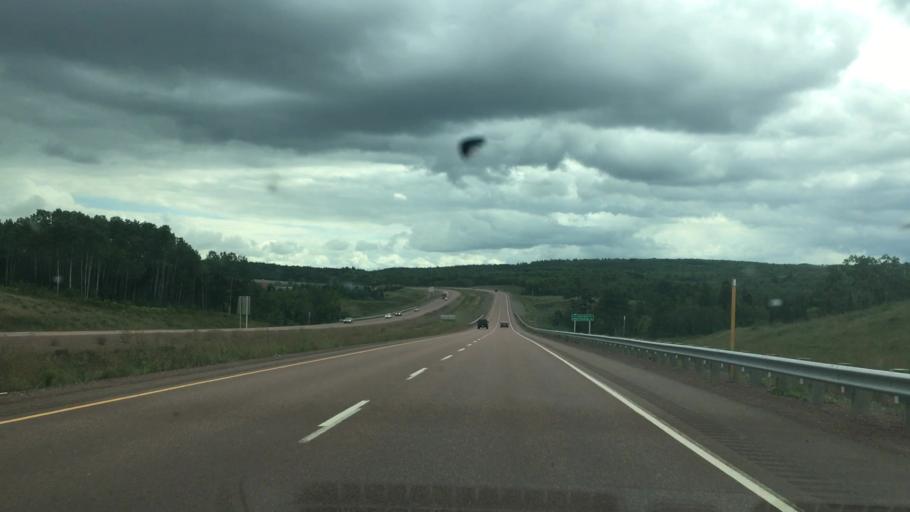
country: CA
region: Nova Scotia
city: Antigonish
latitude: 45.6056
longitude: -61.9558
